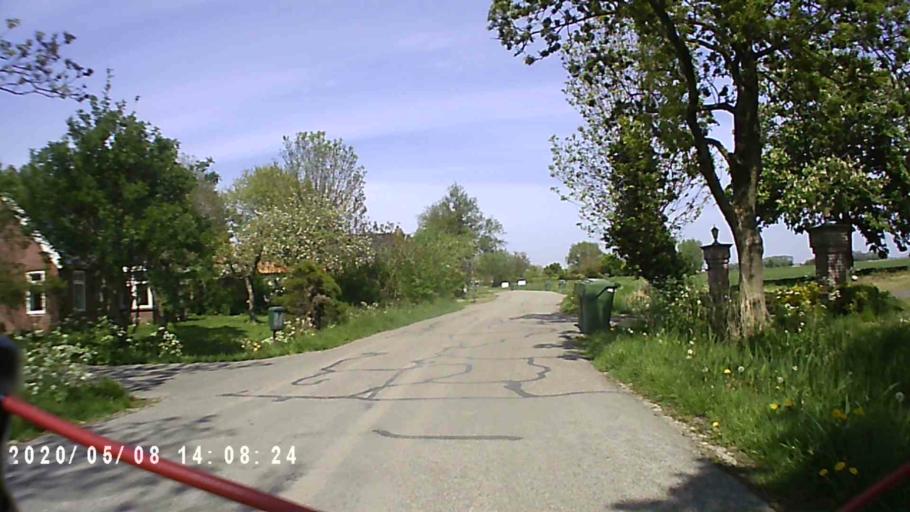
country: NL
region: Groningen
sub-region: Gemeente Appingedam
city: Appingedam
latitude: 53.3412
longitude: 6.7999
